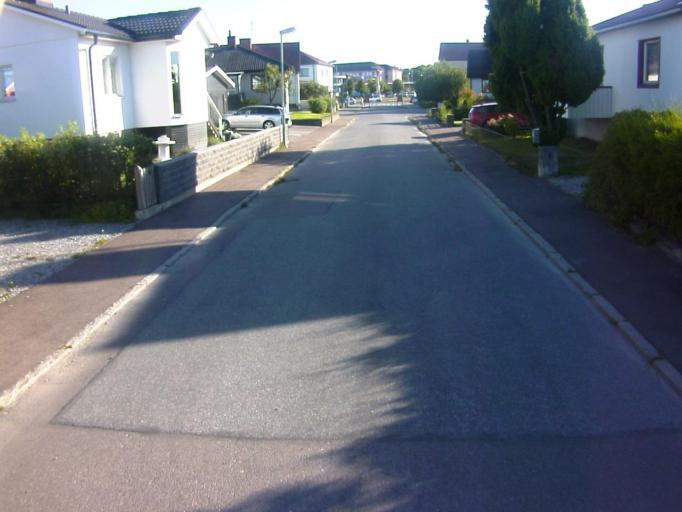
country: SE
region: Soedermanland
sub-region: Eskilstuna Kommun
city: Eskilstuna
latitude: 59.3769
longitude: 16.5304
